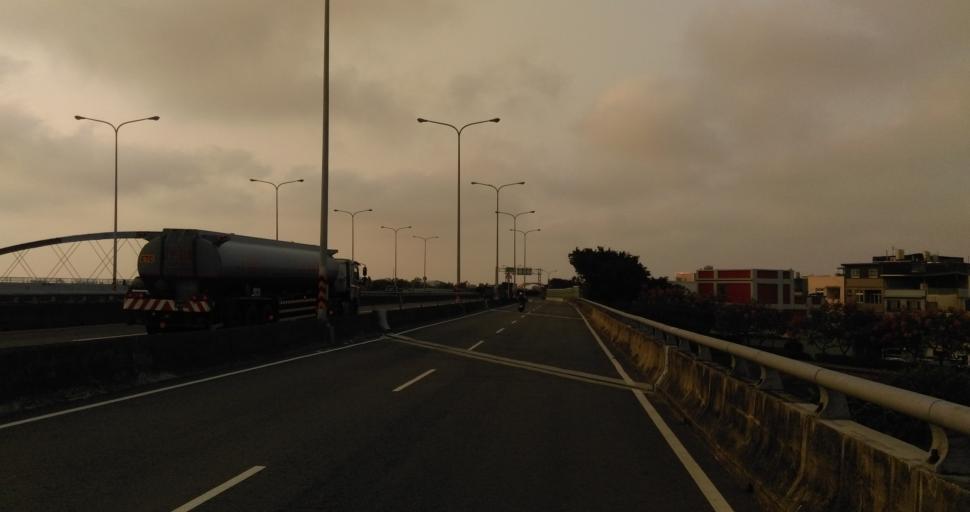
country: TW
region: Taiwan
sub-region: Hsinchu
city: Hsinchu
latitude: 24.8050
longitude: 120.9194
